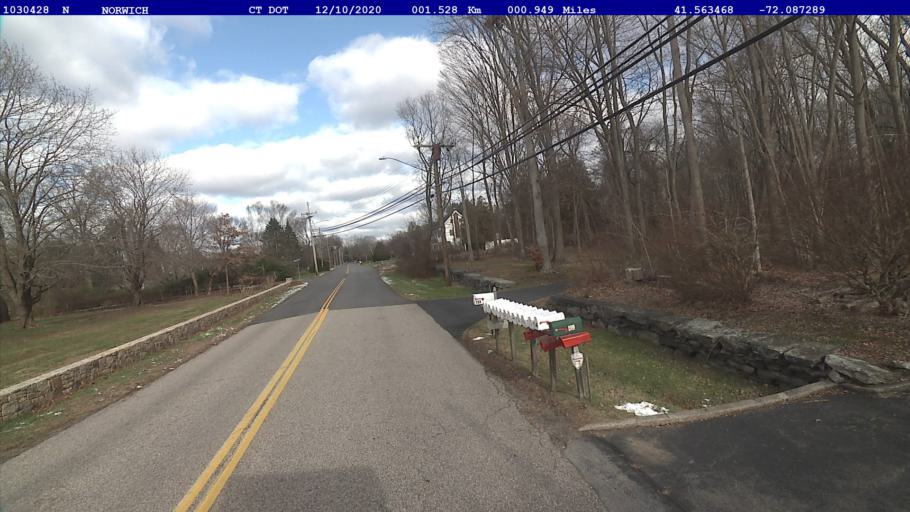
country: US
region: Connecticut
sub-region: New London County
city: Norwich
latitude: 41.5635
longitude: -72.0873
